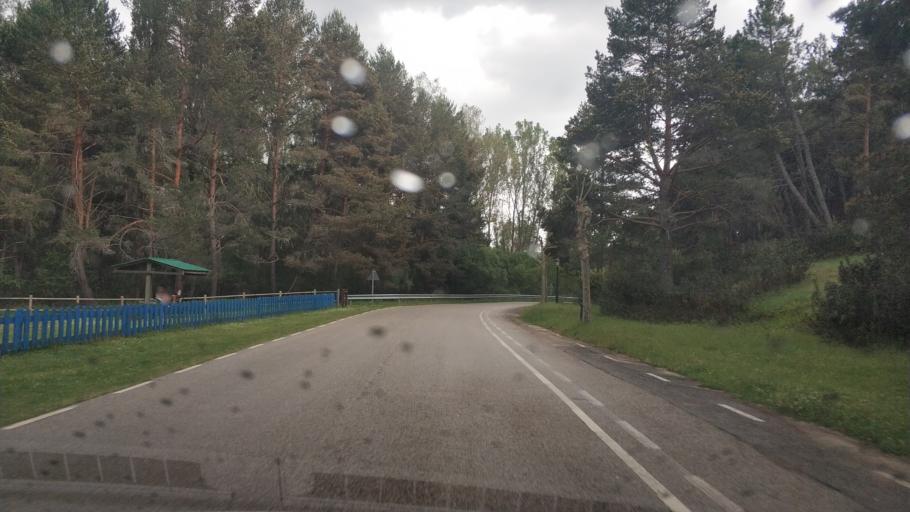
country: ES
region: Castille and Leon
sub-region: Provincia de Soria
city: San Leonardo de Yague
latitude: 41.8365
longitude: -3.0661
